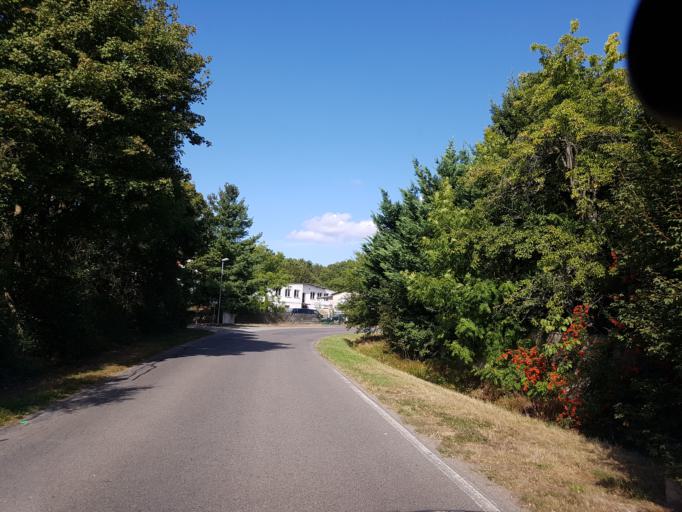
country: DE
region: Brandenburg
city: Sonnewalde
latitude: 51.6977
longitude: 13.6484
